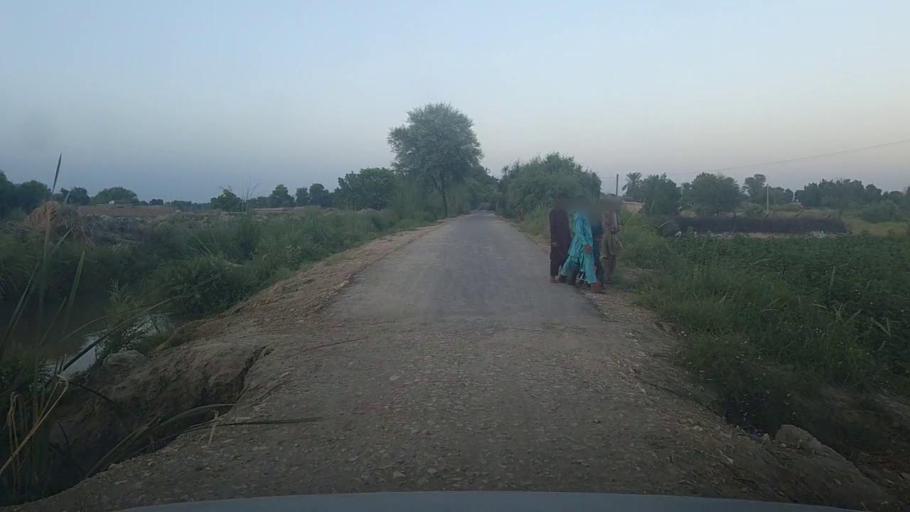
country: PK
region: Sindh
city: Khairpur
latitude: 28.0953
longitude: 69.7364
